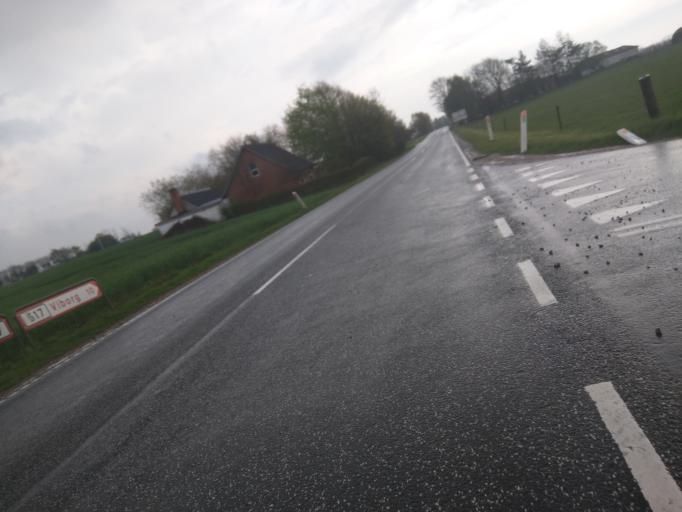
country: DK
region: Central Jutland
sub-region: Viborg Kommune
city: Bjerringbro
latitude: 56.4761
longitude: 9.5580
